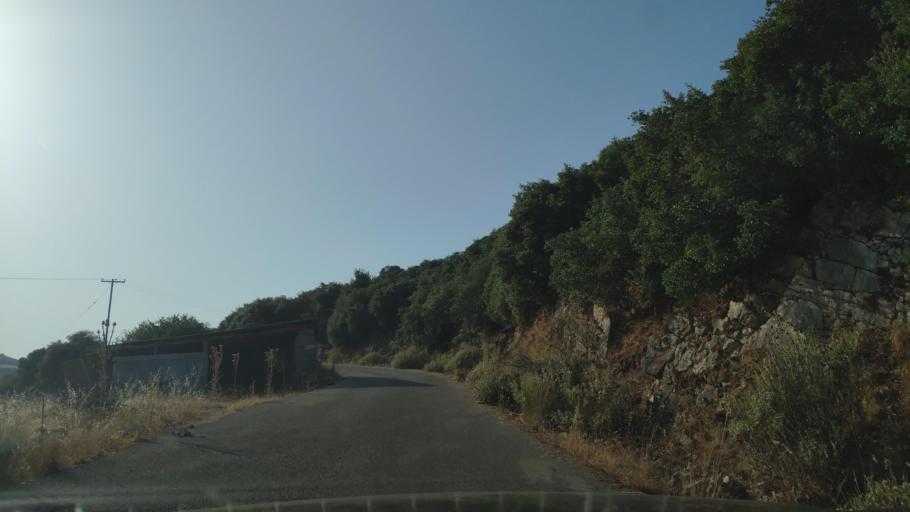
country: GR
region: West Greece
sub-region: Nomos Aitolias kai Akarnanias
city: Monastirakion
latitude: 38.8436
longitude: 20.9748
